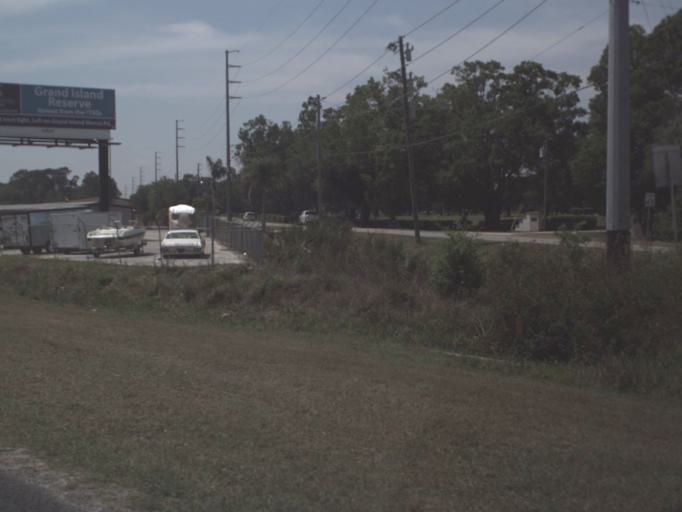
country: US
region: Florida
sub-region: Lake County
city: Eustis
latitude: 28.8834
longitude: -81.6874
